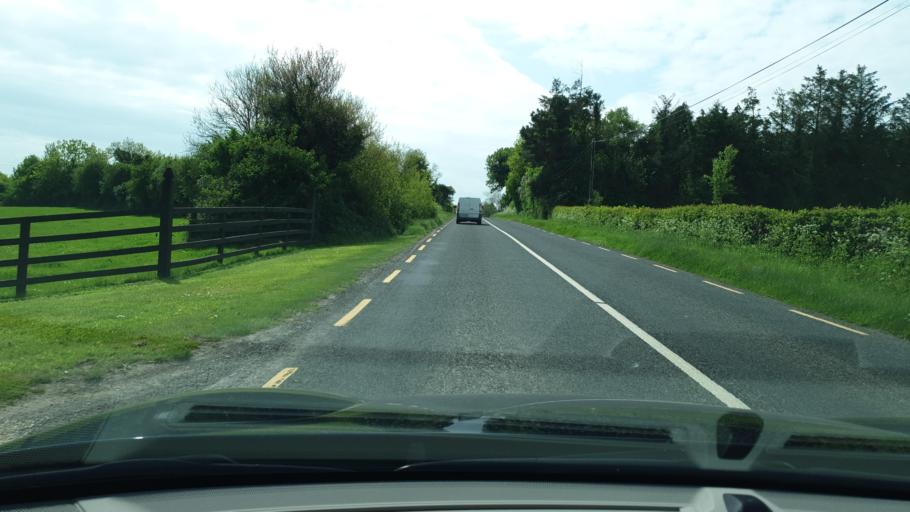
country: IE
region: Leinster
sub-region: An Mhi
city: Navan
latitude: 53.7765
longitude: -6.7260
